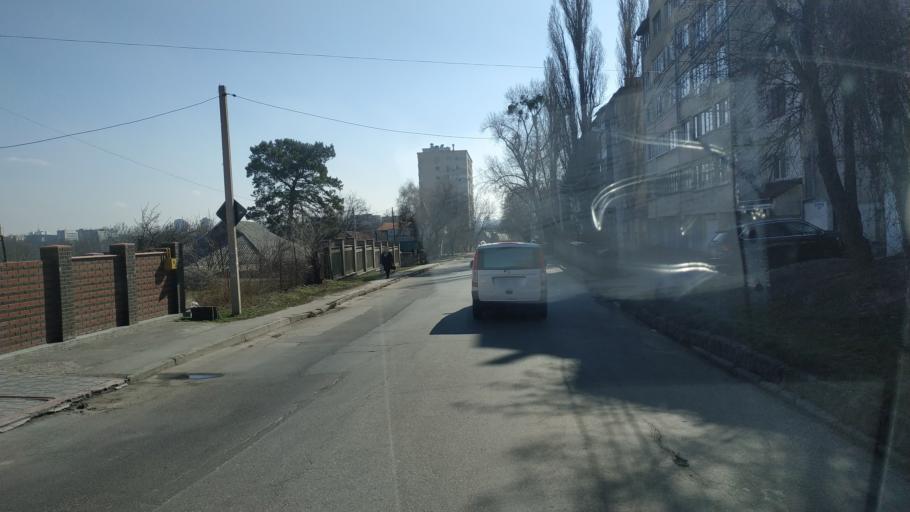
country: MD
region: Chisinau
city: Chisinau
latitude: 47.0321
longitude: 28.7993
